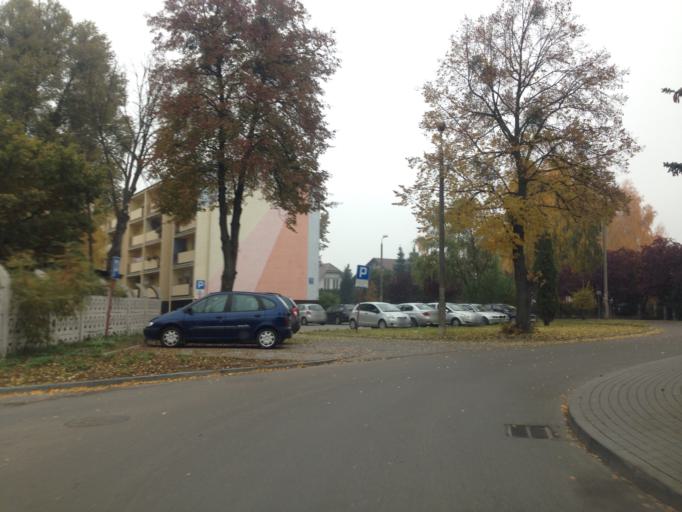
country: PL
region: Kujawsko-Pomorskie
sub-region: Powiat brodnicki
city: Brodnica
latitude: 53.2722
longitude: 19.4038
